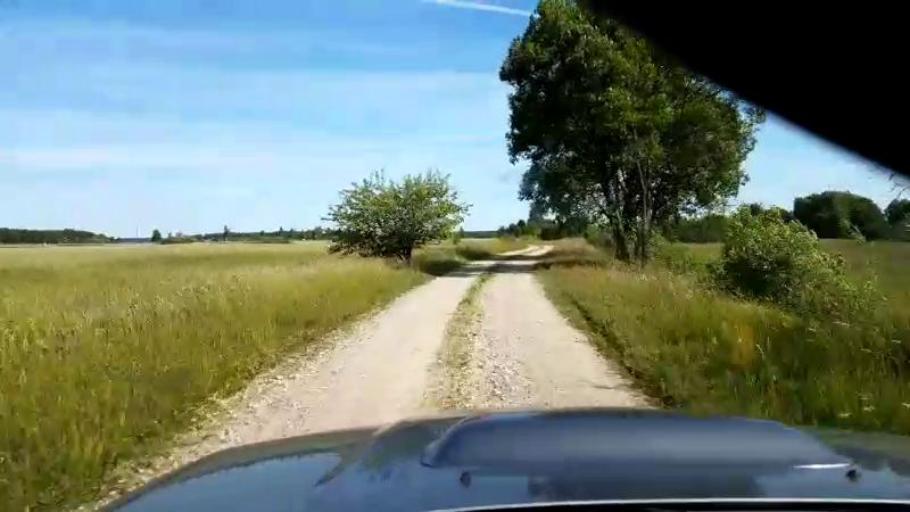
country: EE
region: Paernumaa
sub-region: Sauga vald
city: Sauga
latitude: 58.4839
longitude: 24.5302
